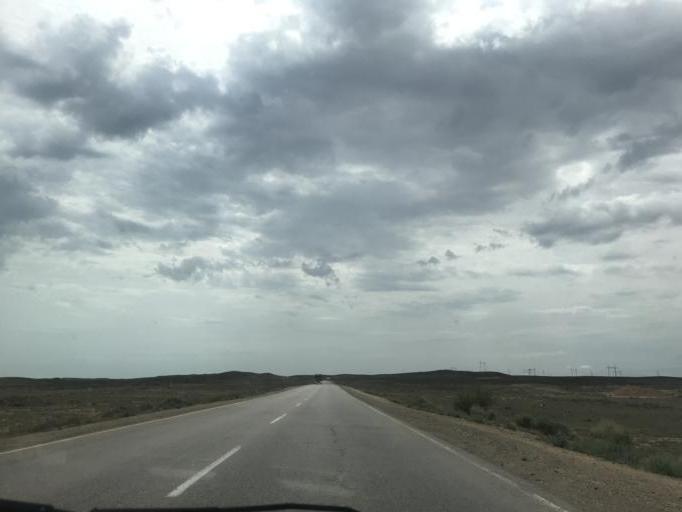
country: KZ
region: Zhambyl
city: Mynaral
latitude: 45.5209
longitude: 73.4884
